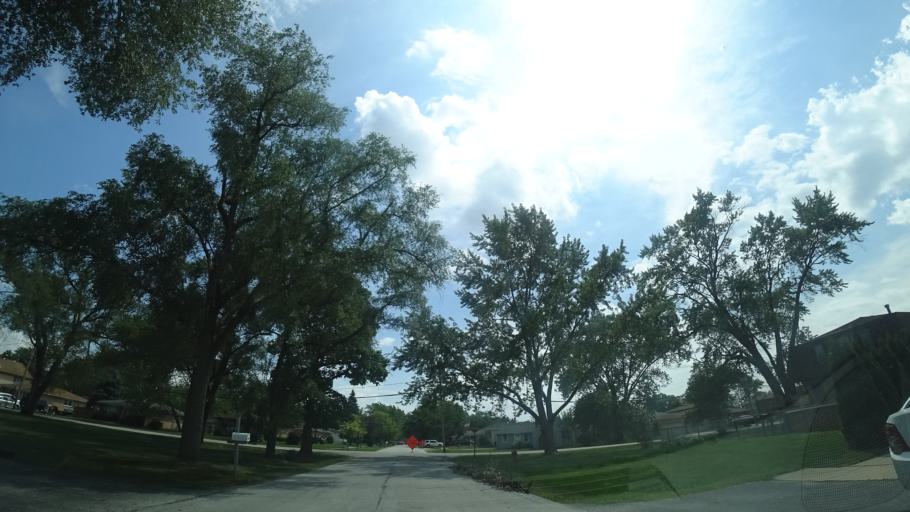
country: US
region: Illinois
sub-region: Cook County
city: Alsip
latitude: 41.6784
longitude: -87.7466
